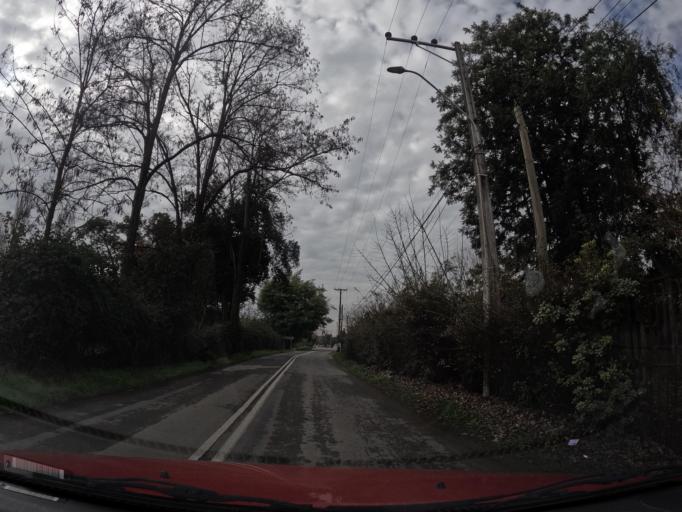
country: CL
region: Maule
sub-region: Provincia de Linares
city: Linares
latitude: -35.8552
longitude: -71.6140
